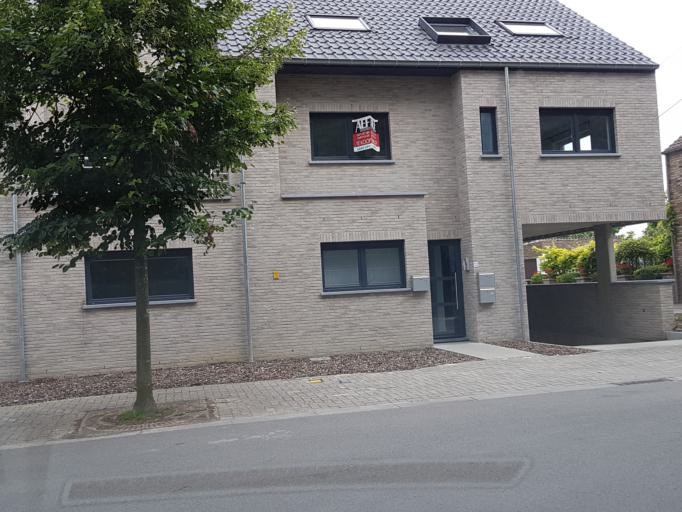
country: BE
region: Flanders
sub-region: Provincie Vlaams-Brabant
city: Zaventem
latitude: 50.9159
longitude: 4.4746
